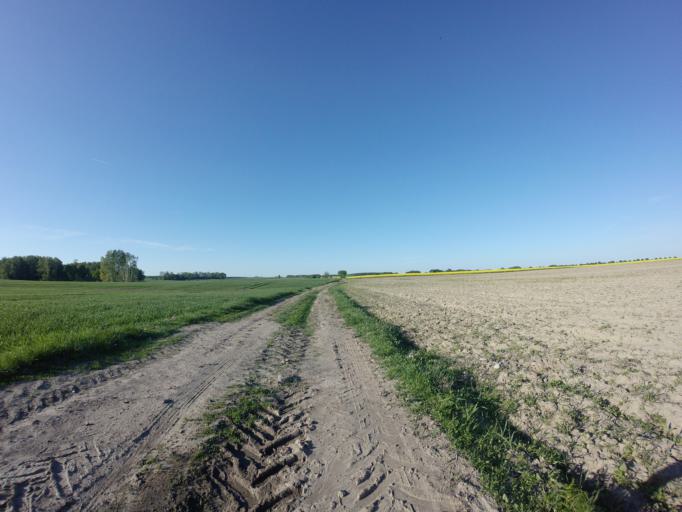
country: PL
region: West Pomeranian Voivodeship
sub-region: Powiat choszczenski
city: Choszczno
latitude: 53.1395
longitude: 15.3603
